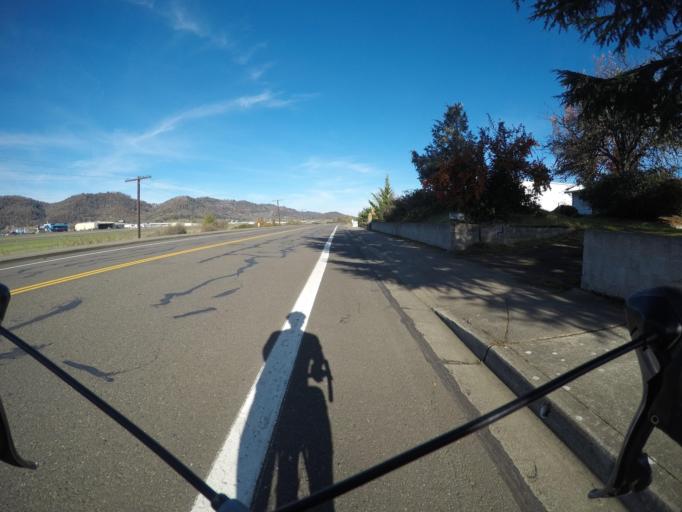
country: US
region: Oregon
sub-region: Douglas County
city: Roseburg
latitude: 43.2339
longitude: -123.3545
